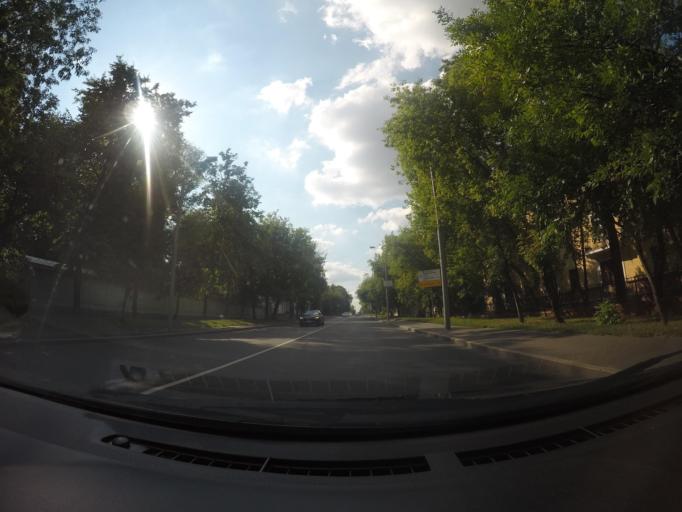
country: RU
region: Moscow
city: Leonovo
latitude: 55.8344
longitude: 37.6473
